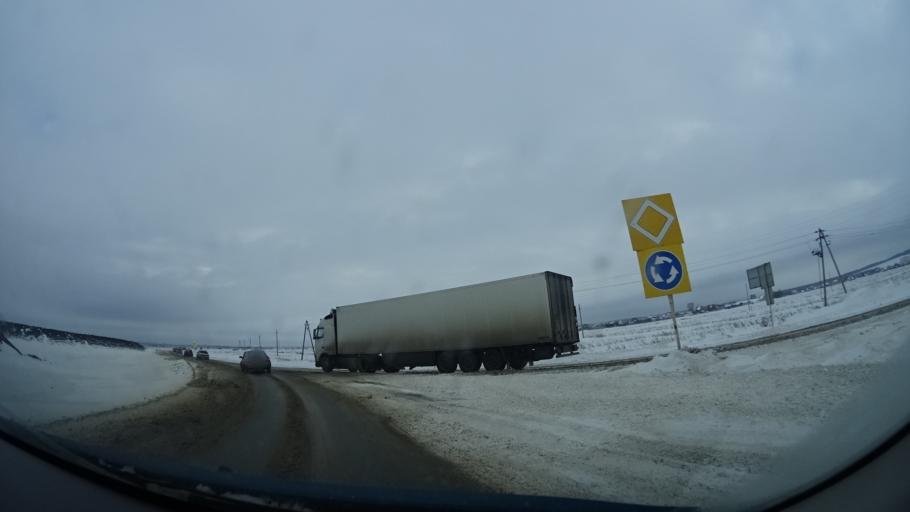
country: RU
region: Bashkortostan
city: Mikhaylovka
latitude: 54.8763
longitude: 55.7114
